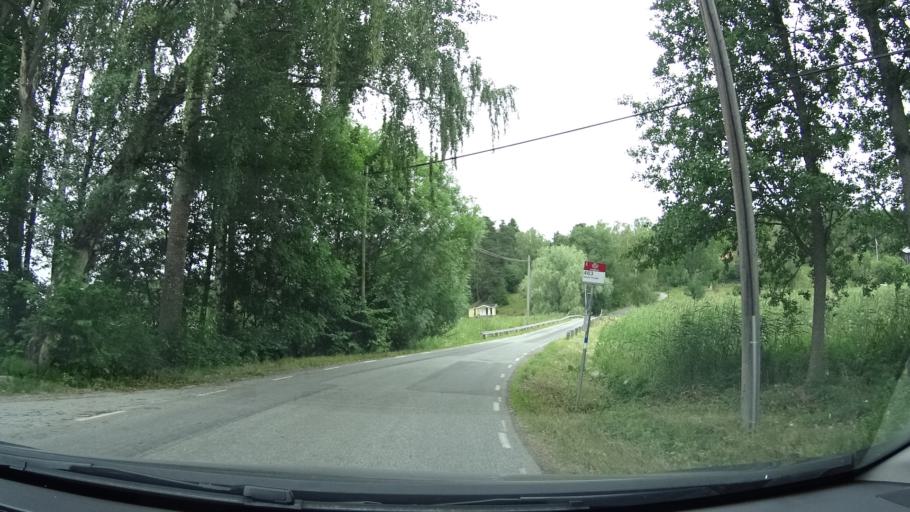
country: SE
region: Stockholm
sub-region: Varmdo Kommun
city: Mortnas
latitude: 59.3705
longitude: 18.4655
